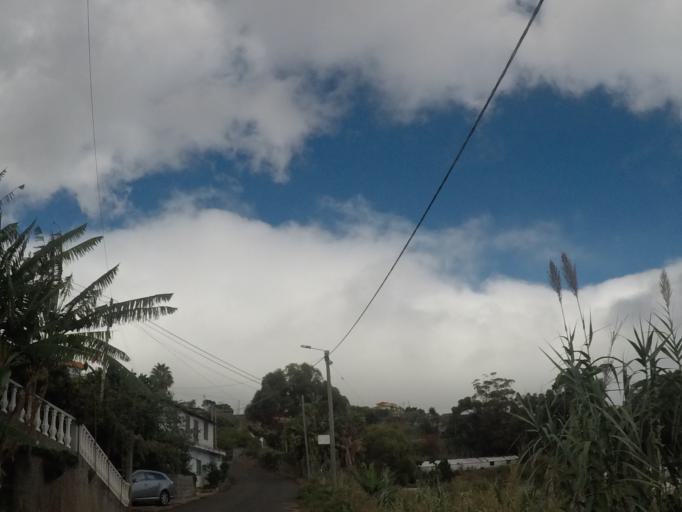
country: PT
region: Madeira
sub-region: Santa Cruz
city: Camacha
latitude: 32.6613
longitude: -16.8272
